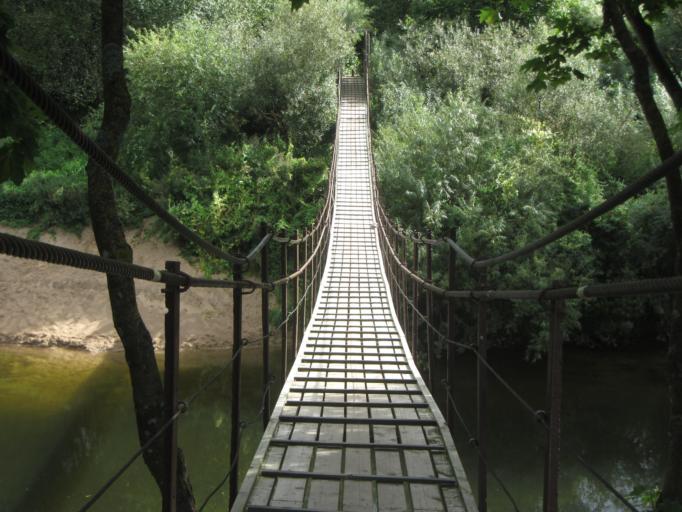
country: LT
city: Priekule
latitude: 55.5944
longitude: 21.2914
